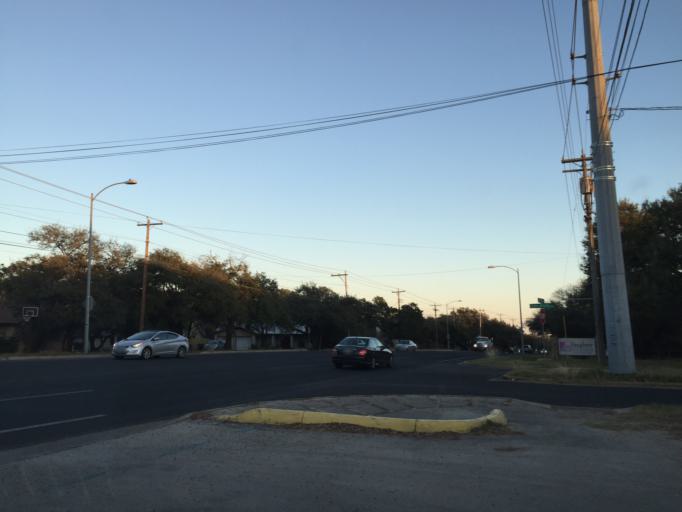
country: US
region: Texas
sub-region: Williamson County
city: Jollyville
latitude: 30.4215
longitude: -97.7545
